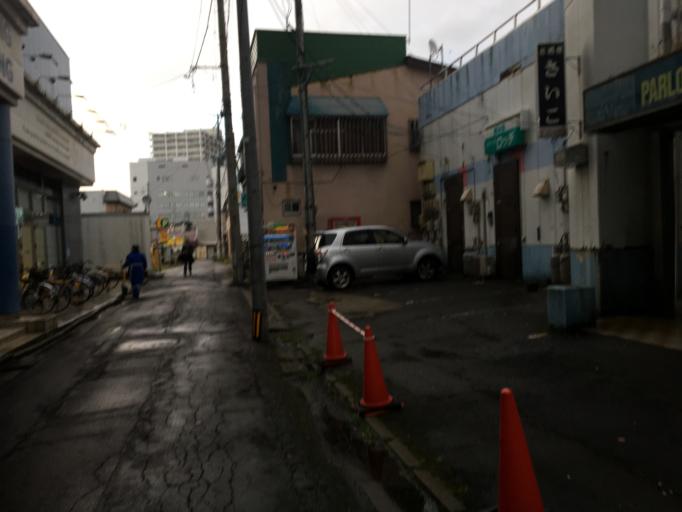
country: JP
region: Aomori
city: Aomori Shi
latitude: 40.8251
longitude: 140.7339
